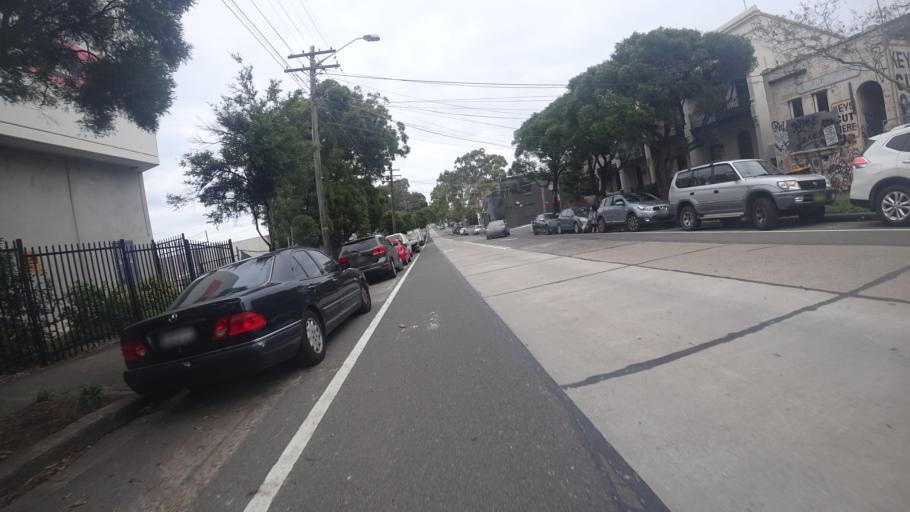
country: AU
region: New South Wales
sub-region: Marrickville
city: Newtown
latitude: -33.9073
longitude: 151.1683
